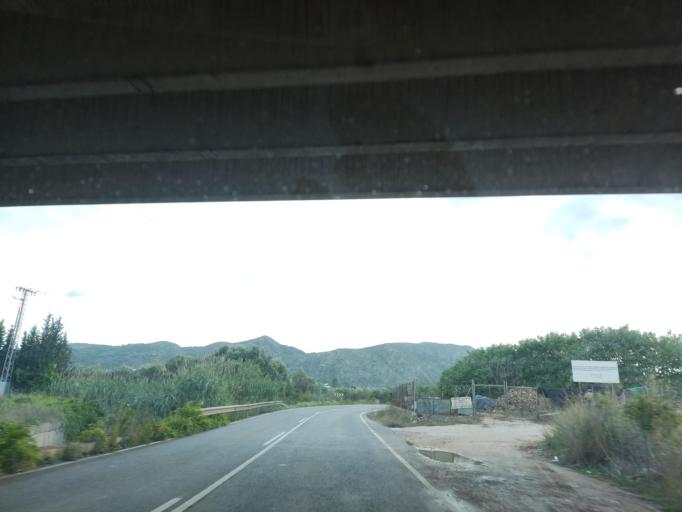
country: ES
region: Valencia
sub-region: Provincia de Alicante
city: Pedreguer
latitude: 38.8040
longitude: 0.0334
